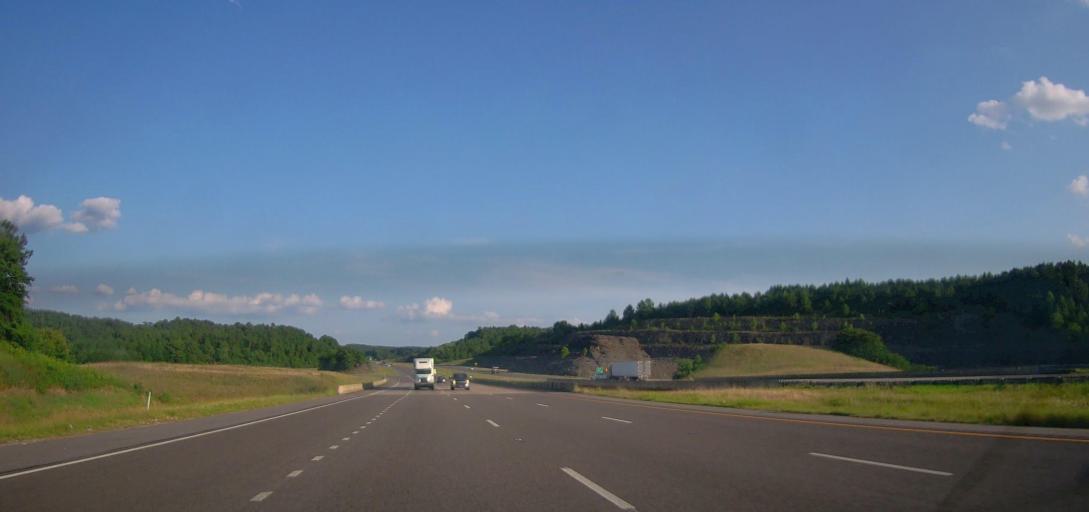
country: US
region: Alabama
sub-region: Walker County
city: Cordova
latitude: 33.7420
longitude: -87.2008
